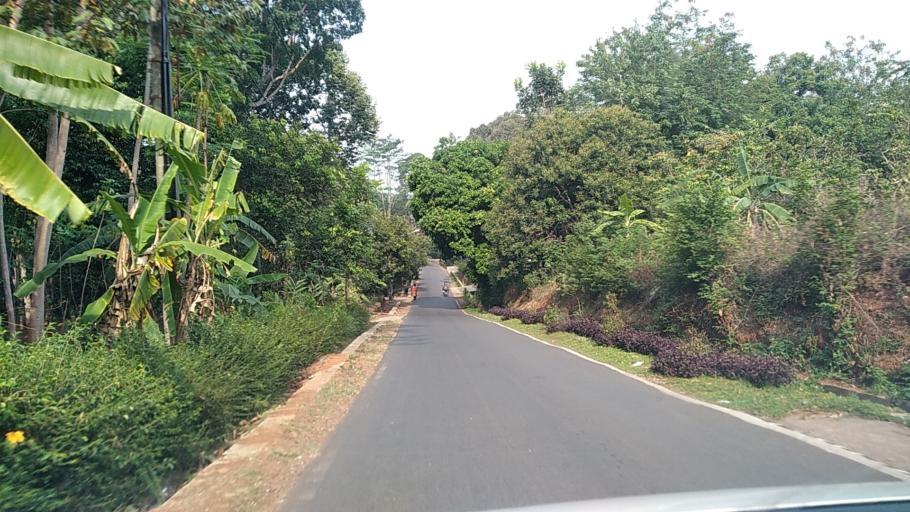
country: ID
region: Central Java
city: Ungaran
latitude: -7.0939
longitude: 110.3909
